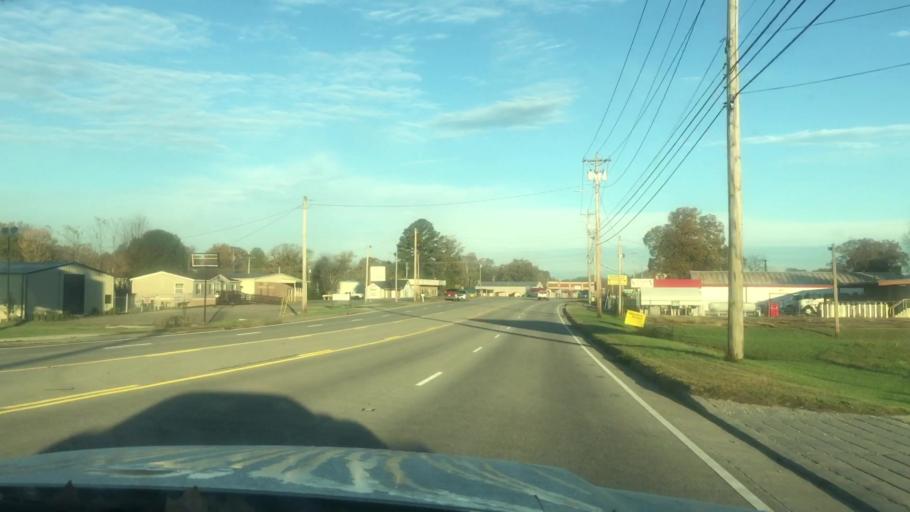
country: US
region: Tennessee
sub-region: Coffee County
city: Tullahoma
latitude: 35.3488
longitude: -86.1993
